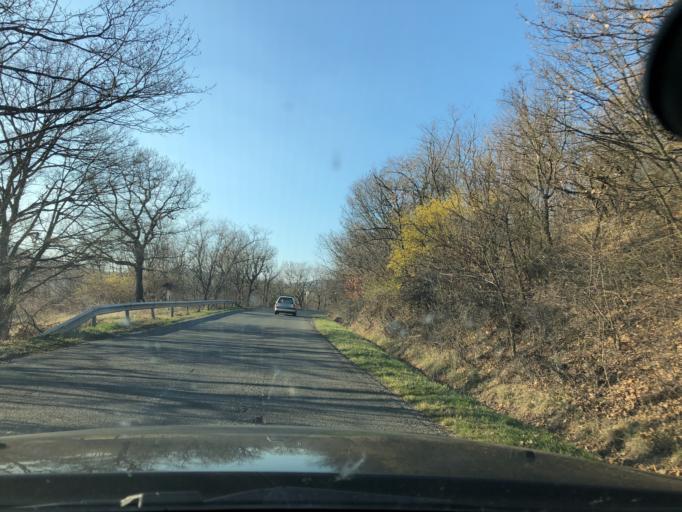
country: HU
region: Nograd
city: Paszto
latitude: 47.9241
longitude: 19.6303
